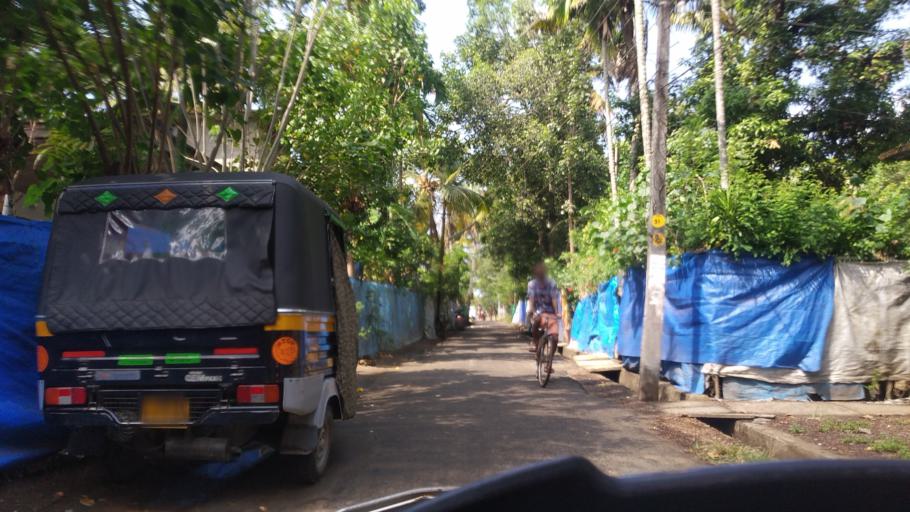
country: IN
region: Kerala
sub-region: Thrissur District
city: Kodungallur
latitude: 10.1356
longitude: 76.2099
